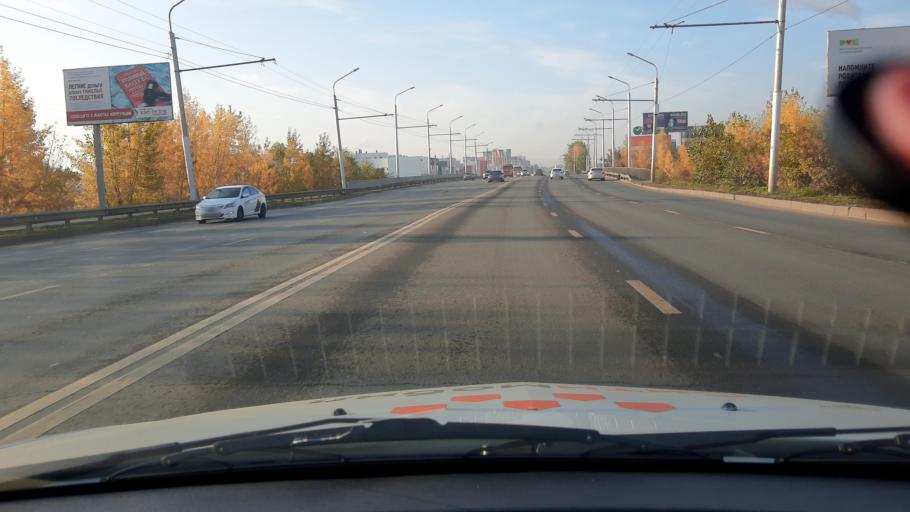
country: RU
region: Bashkortostan
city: Ufa
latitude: 54.7871
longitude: 56.0774
